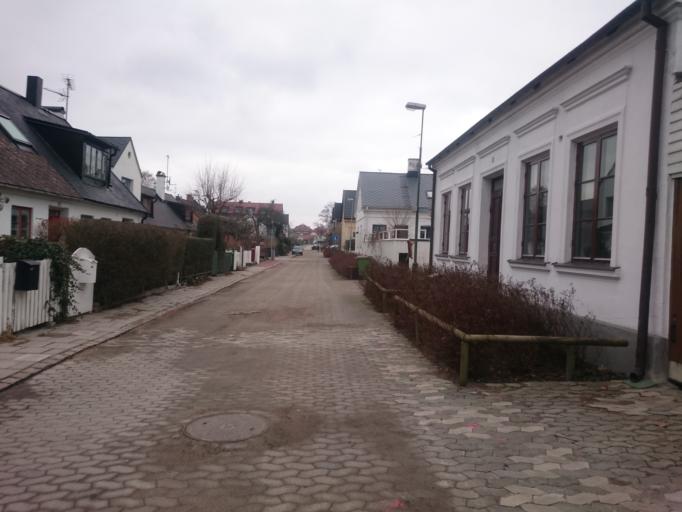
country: SE
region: Skane
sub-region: Malmo
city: Bunkeflostrand
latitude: 55.5851
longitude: 12.9329
